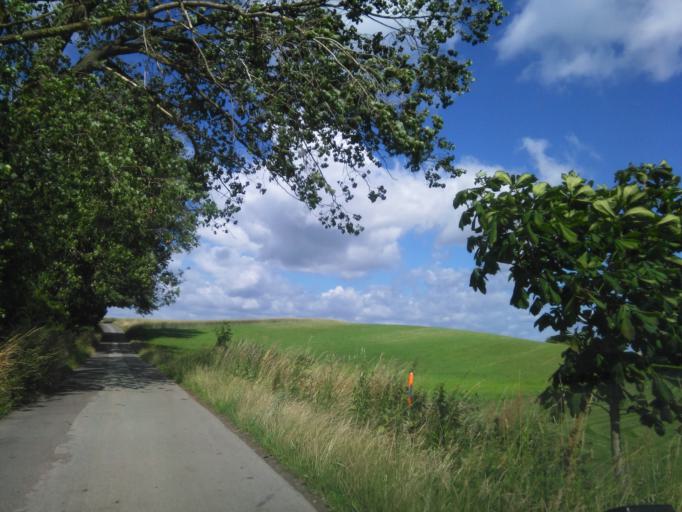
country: DK
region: Central Jutland
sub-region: Syddjurs Kommune
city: Ronde
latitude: 56.1723
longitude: 10.4197
